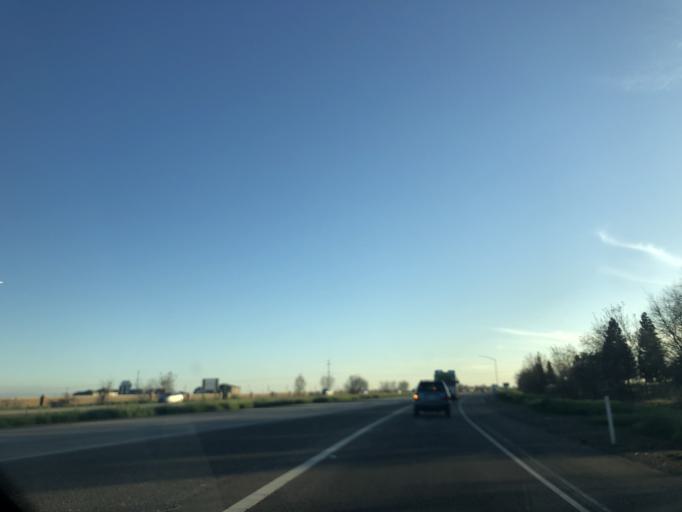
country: US
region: California
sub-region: Yolo County
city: Woodland
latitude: 38.6592
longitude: -121.7526
